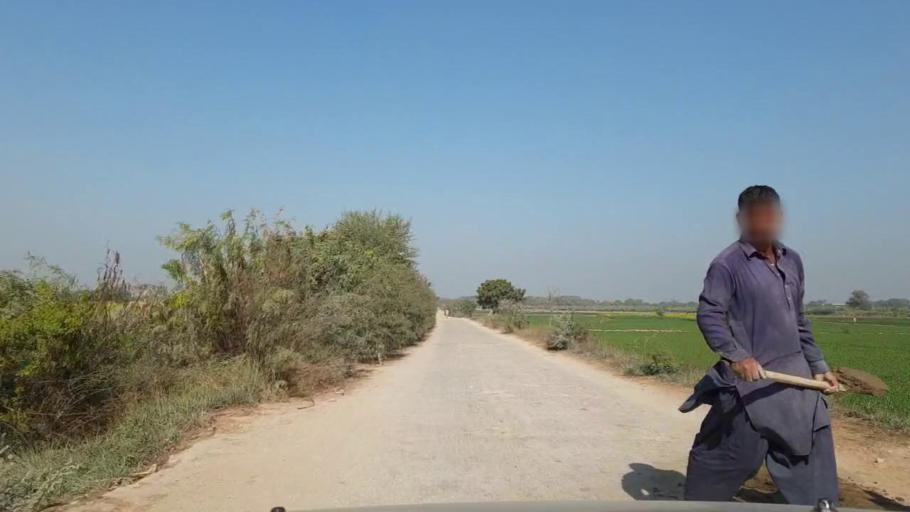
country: PK
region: Sindh
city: Matiari
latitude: 25.5808
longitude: 68.6034
